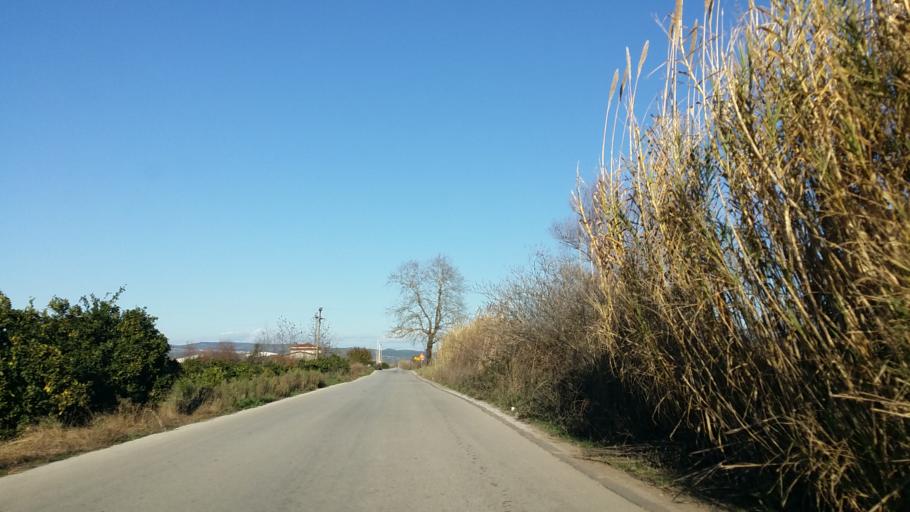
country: GR
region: West Greece
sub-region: Nomos Aitolias kai Akarnanias
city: Lepenou
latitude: 38.6376
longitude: 21.2465
